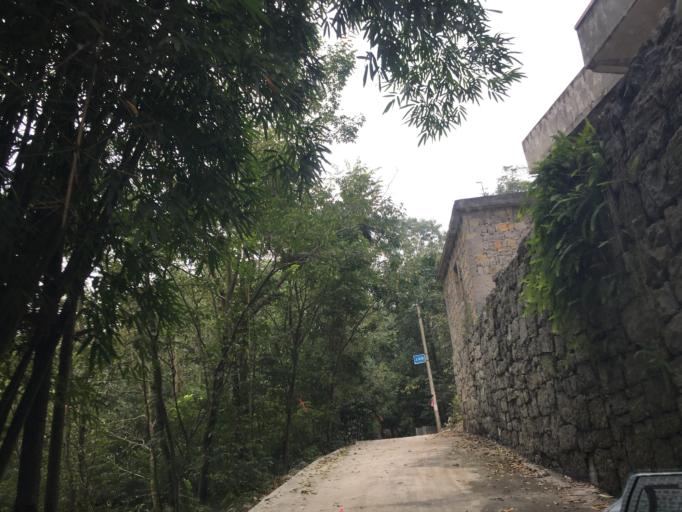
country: CN
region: Guangxi Zhuangzu Zizhiqu
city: Xinzhou
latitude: 25.5244
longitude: 105.5969
